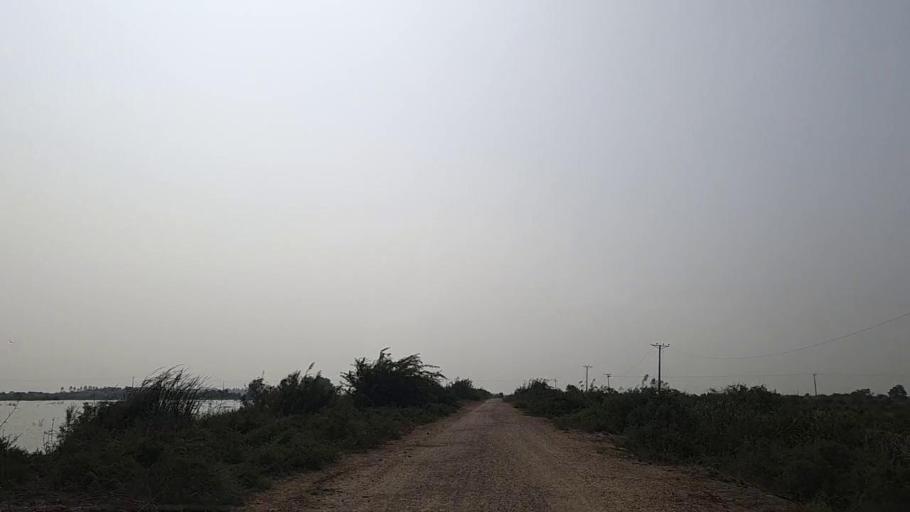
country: PK
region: Sindh
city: Thatta
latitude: 24.6951
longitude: 67.8009
